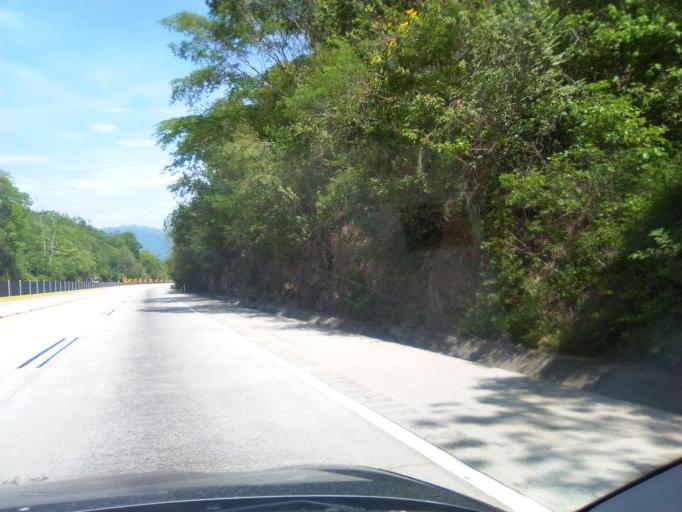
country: MX
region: Guerrero
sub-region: Acapulco de Juarez
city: Kilometro 30
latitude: 16.9562
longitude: -99.7490
